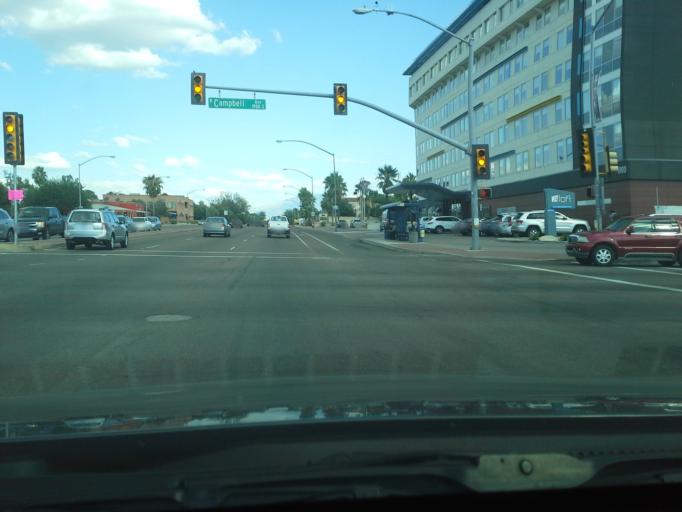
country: US
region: Arizona
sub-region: Pima County
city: Tucson
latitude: 32.2360
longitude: -110.9440
